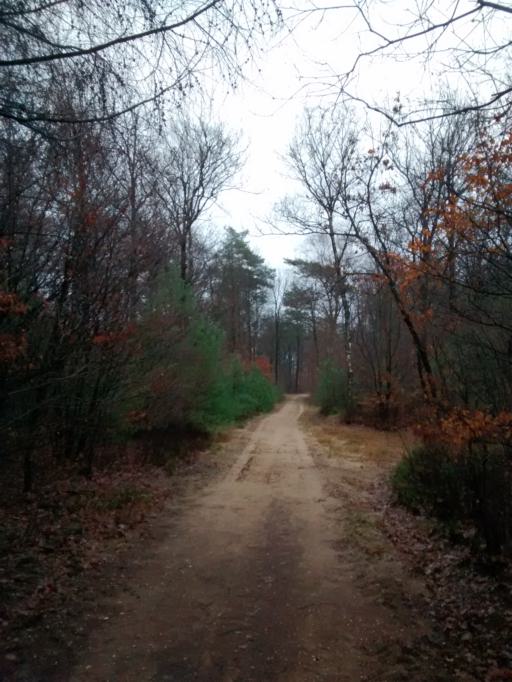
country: NL
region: Gelderland
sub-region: Gemeente Ede
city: Bennekom
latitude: 52.0322
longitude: 5.7115
